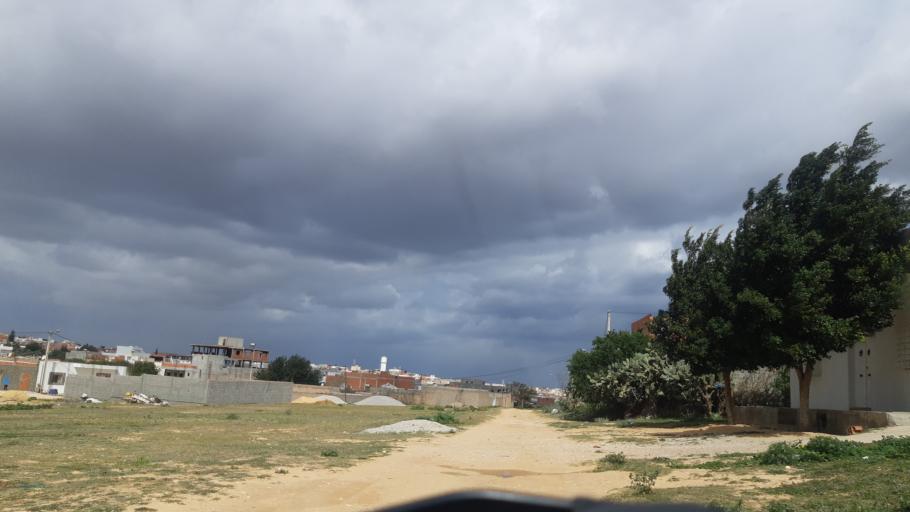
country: TN
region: Susah
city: Akouda
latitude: 35.8586
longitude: 10.5255
